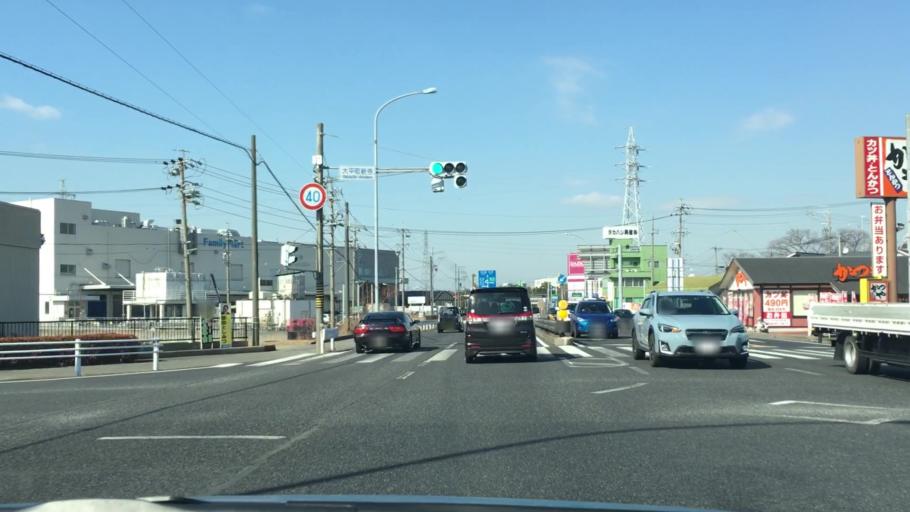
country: JP
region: Aichi
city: Okazaki
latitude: 34.9418
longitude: 137.1921
